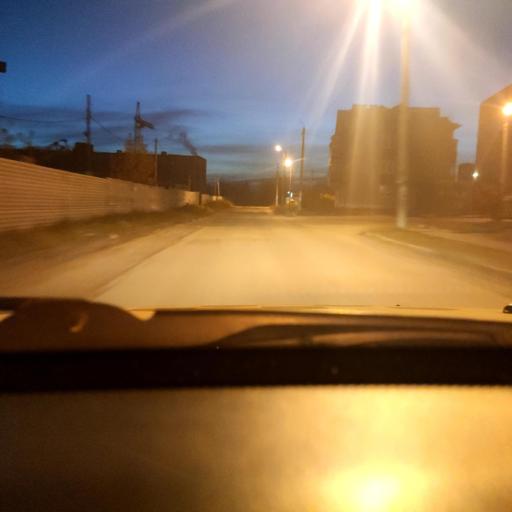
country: RU
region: Perm
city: Ferma
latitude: 57.8974
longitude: 56.3261
